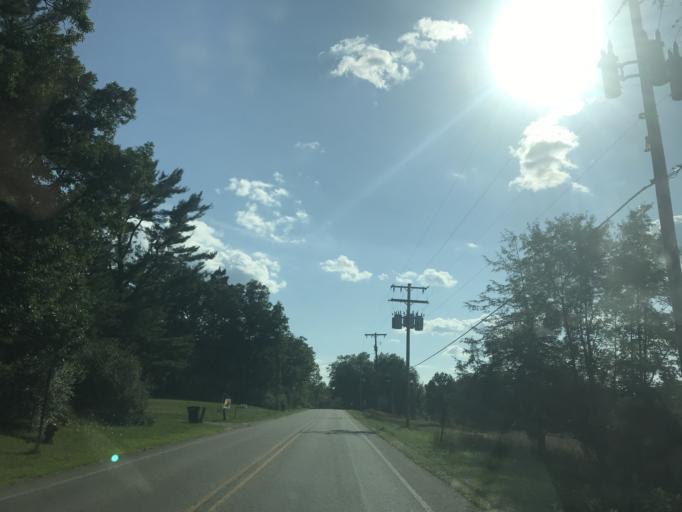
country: US
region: Michigan
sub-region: Newaygo County
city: Newaygo
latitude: 43.4255
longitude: -85.7862
